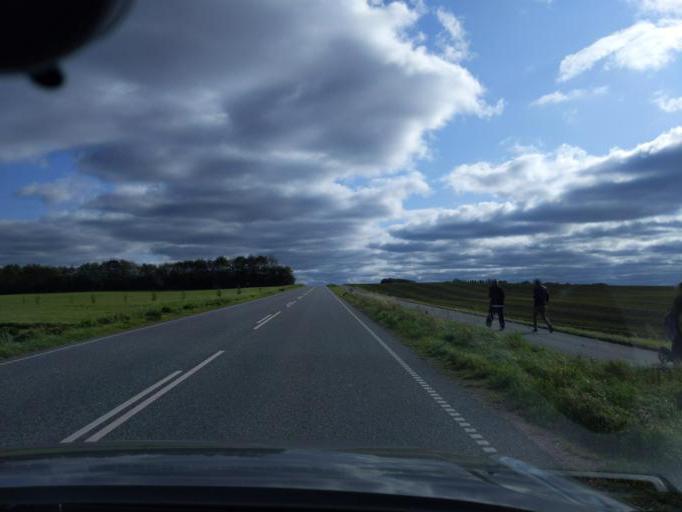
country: DK
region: North Denmark
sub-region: Mariagerfjord Kommune
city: Hobro
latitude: 56.5224
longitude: 9.7320
